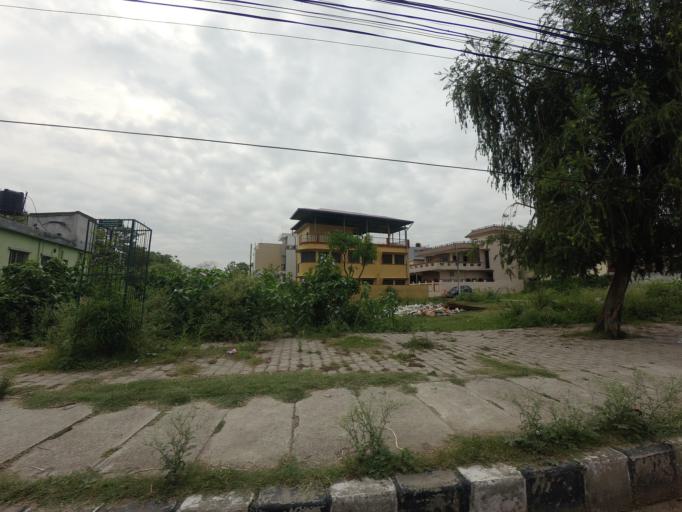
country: NP
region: Western Region
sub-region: Lumbini Zone
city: Bhairahawa
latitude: 27.4967
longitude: 83.4472
